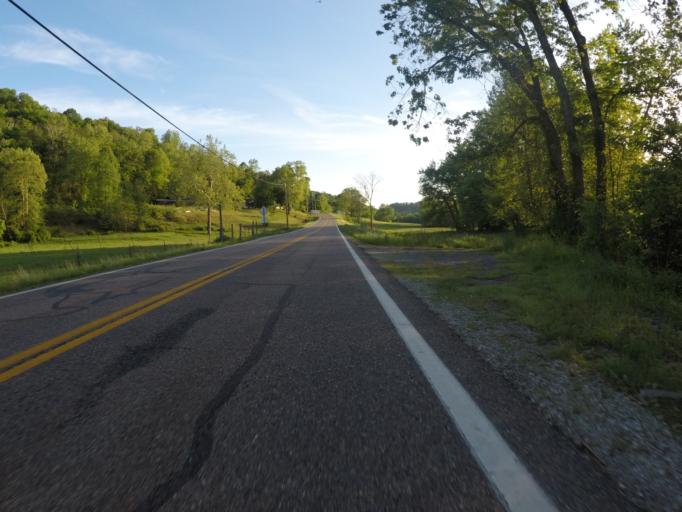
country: US
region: West Virginia
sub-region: Cabell County
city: Huntington
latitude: 38.5095
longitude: -82.4753
